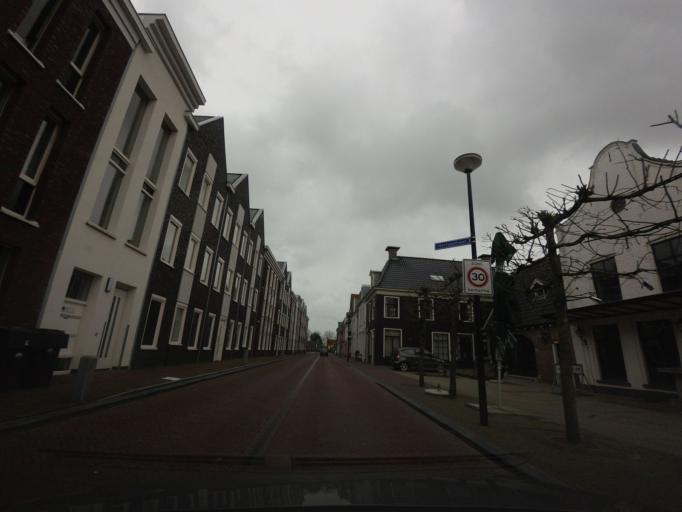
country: NL
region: Friesland
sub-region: Gemeente Franekeradeel
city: Franeker
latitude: 53.1862
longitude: 5.5386
